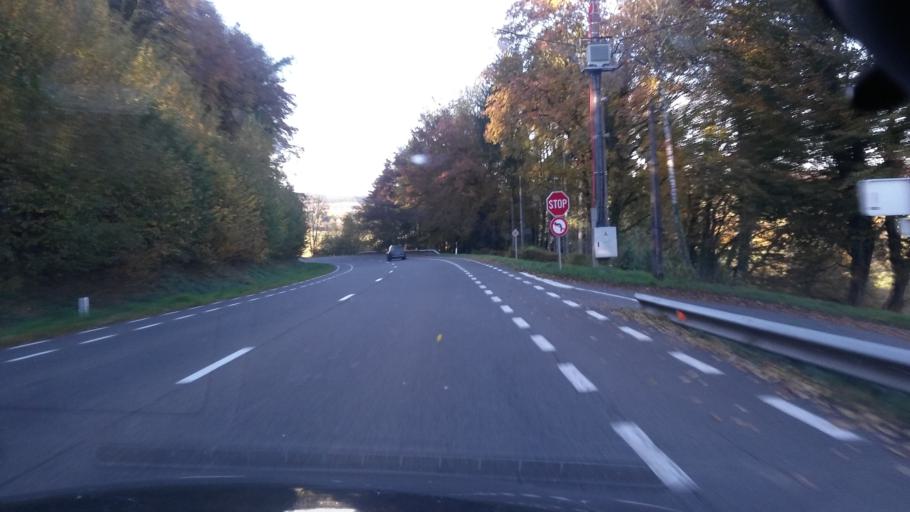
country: BE
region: Wallonia
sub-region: Province du Luxembourg
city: Florenville
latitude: 49.7088
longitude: 5.2591
